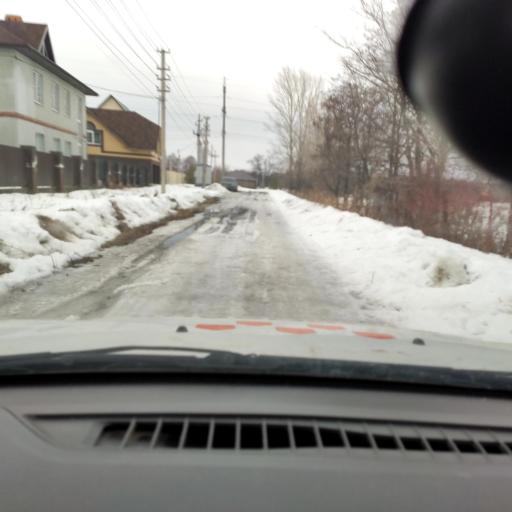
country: RU
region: Bashkortostan
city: Ufa
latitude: 54.5270
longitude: 55.9192
